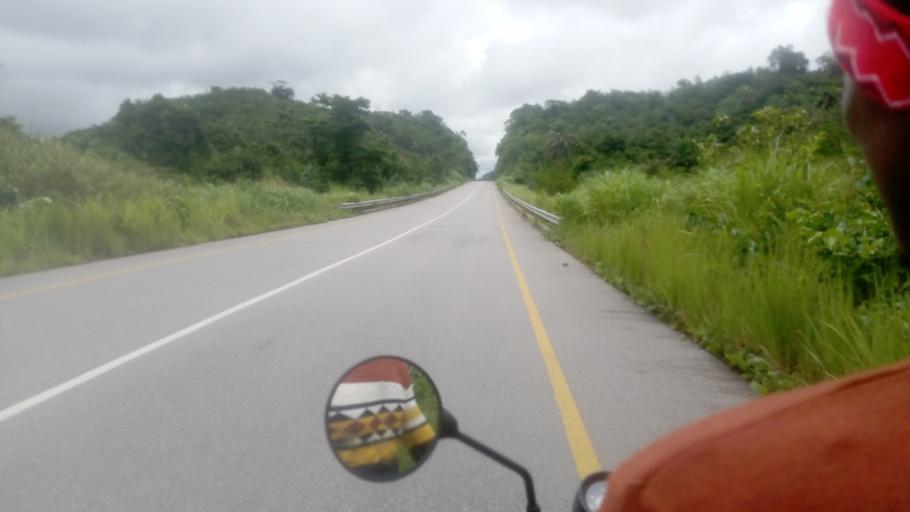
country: SL
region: Northern Province
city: Masaka
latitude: 8.6459
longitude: -11.7480
